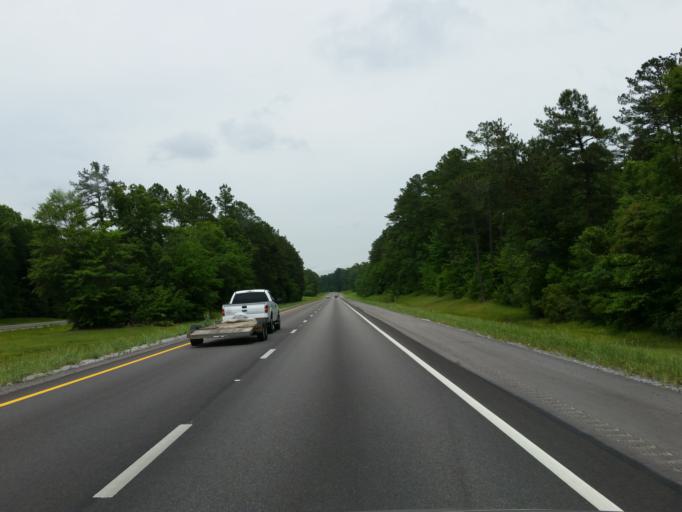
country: US
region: Mississippi
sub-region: Jones County
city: Sharon
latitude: 31.7566
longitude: -89.0677
